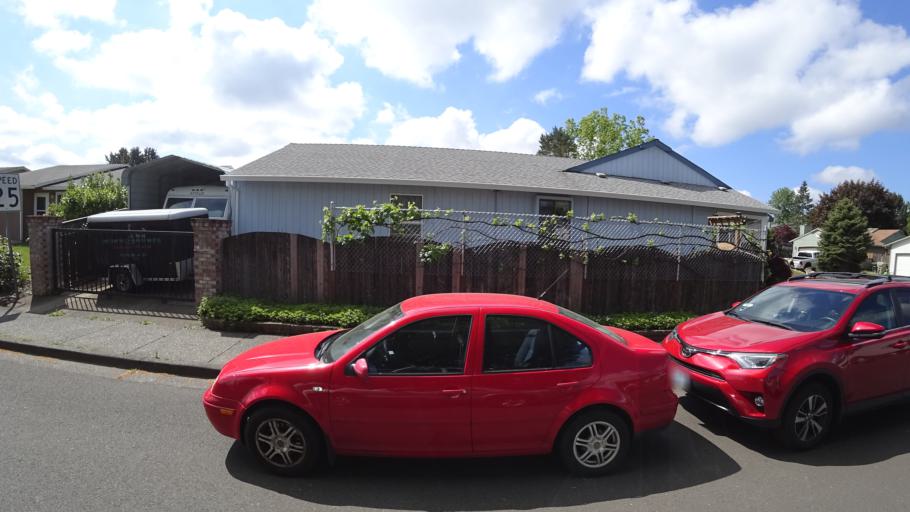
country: US
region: Oregon
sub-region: Washington County
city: Aloha
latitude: 45.5102
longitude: -122.8929
